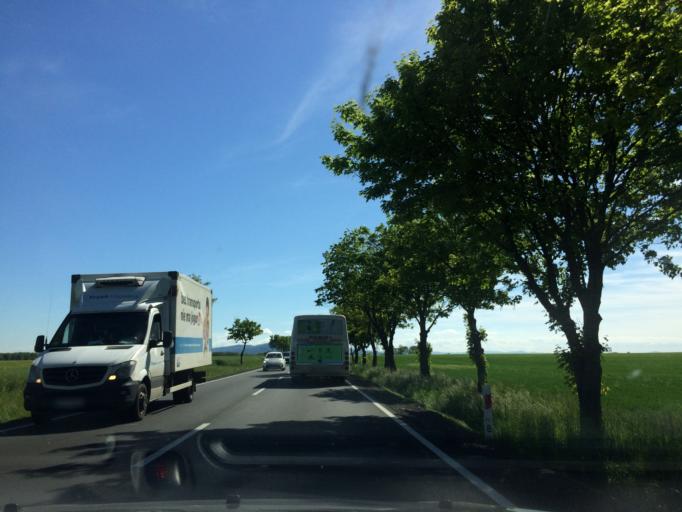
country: PL
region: Lower Silesian Voivodeship
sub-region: Powiat wroclawski
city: Gniechowice
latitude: 50.9807
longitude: 16.8170
